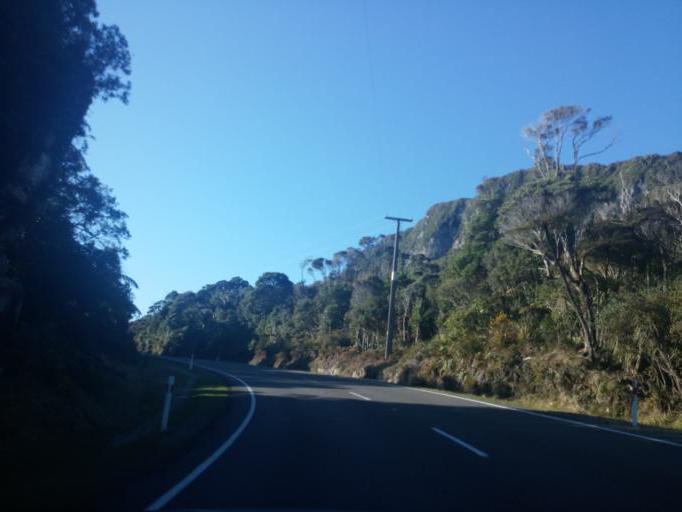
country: NZ
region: West Coast
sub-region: Grey District
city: Greymouth
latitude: -42.0975
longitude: 171.3427
